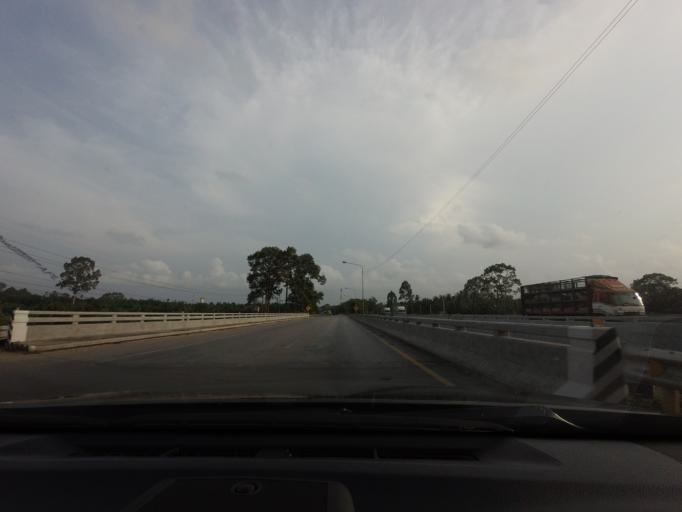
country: TH
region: Chumphon
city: Lamae
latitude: 9.7706
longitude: 99.0792
